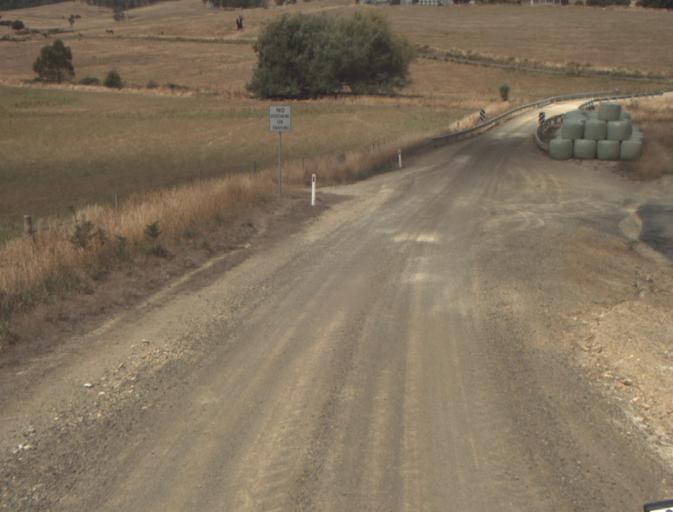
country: AU
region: Tasmania
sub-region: Launceston
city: Mayfield
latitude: -41.2109
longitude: 147.1426
